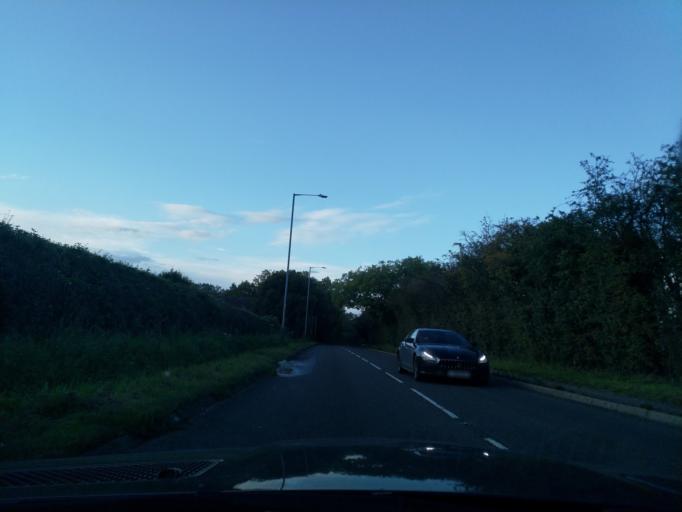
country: GB
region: England
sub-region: Warwickshire
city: Henley in Arden
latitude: 52.3386
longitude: -1.7732
